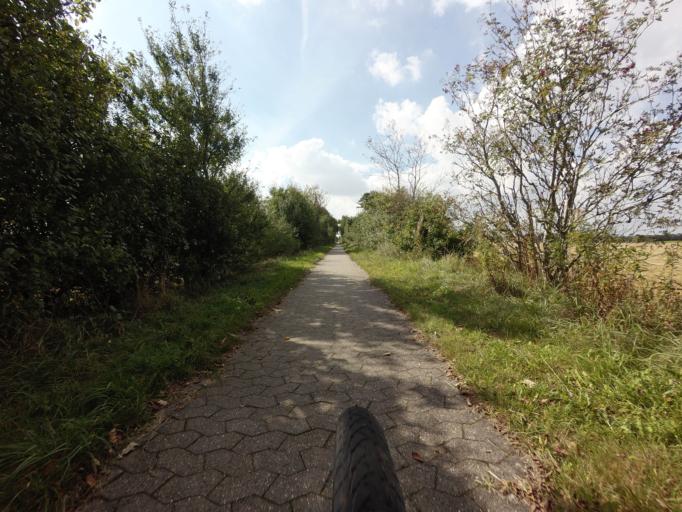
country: DK
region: Central Jutland
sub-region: Viborg Kommune
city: Karup
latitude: 56.3358
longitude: 9.2433
